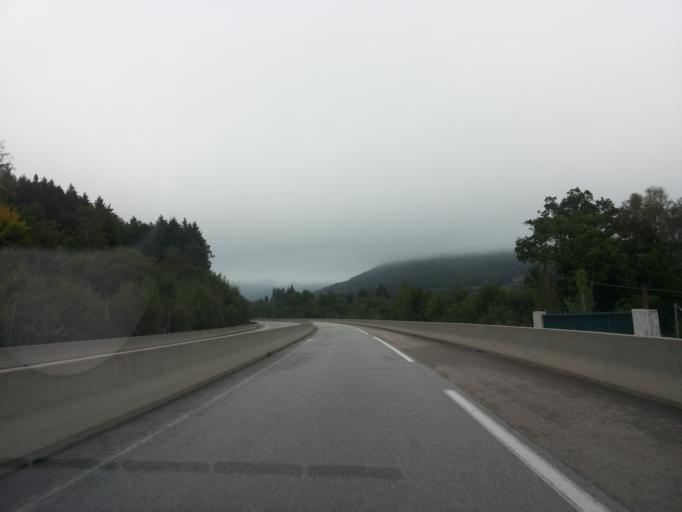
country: FR
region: Lorraine
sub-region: Departement des Vosges
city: Rupt-sur-Moselle
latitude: 47.9273
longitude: 6.6507
